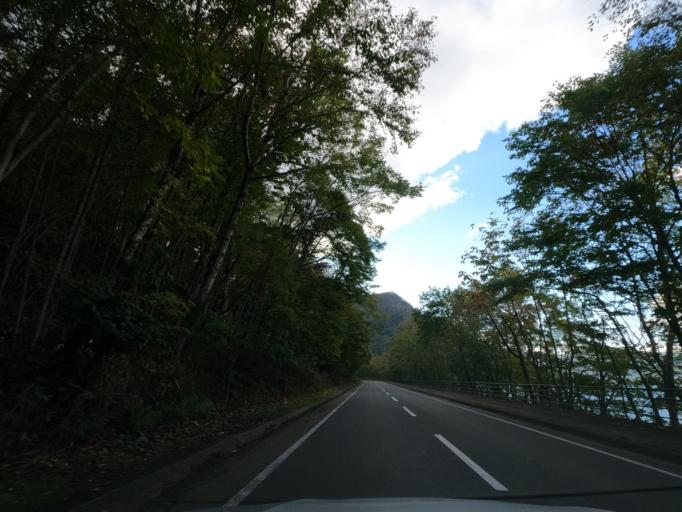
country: JP
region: Hokkaido
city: Shiraoi
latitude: 42.7041
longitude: 141.3023
